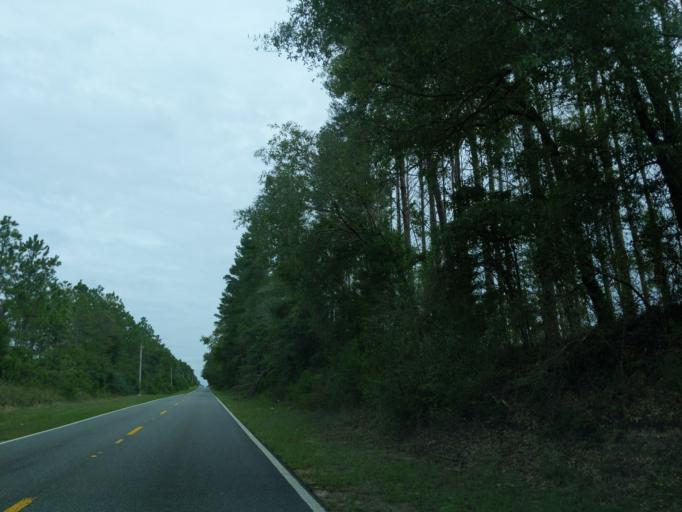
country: US
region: Florida
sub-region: Leon County
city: Woodville
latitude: 30.3763
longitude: -84.2176
